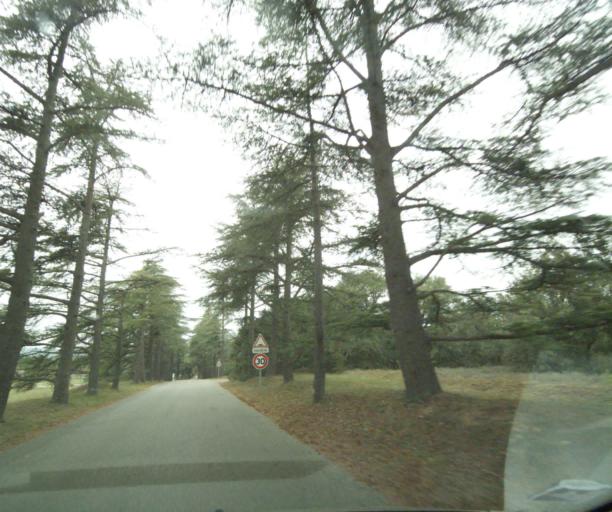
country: FR
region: Provence-Alpes-Cote d'Azur
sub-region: Departement du Var
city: Vinon-sur-Verdon
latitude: 43.7149
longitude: 5.7533
